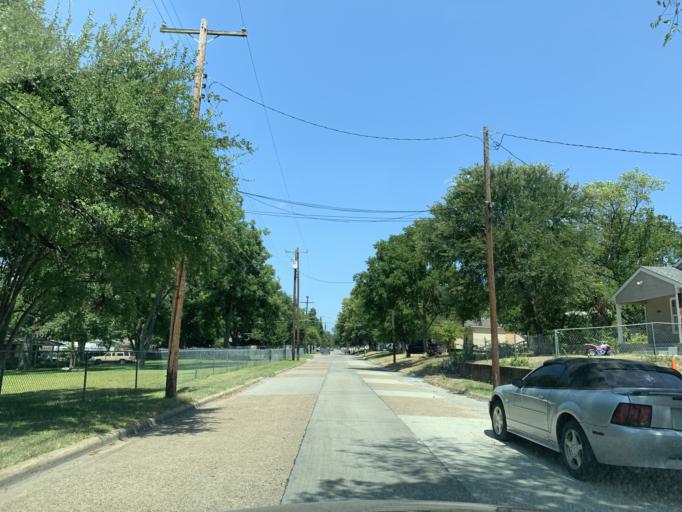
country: US
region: Texas
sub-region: Dallas County
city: Hutchins
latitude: 32.6871
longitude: -96.7937
